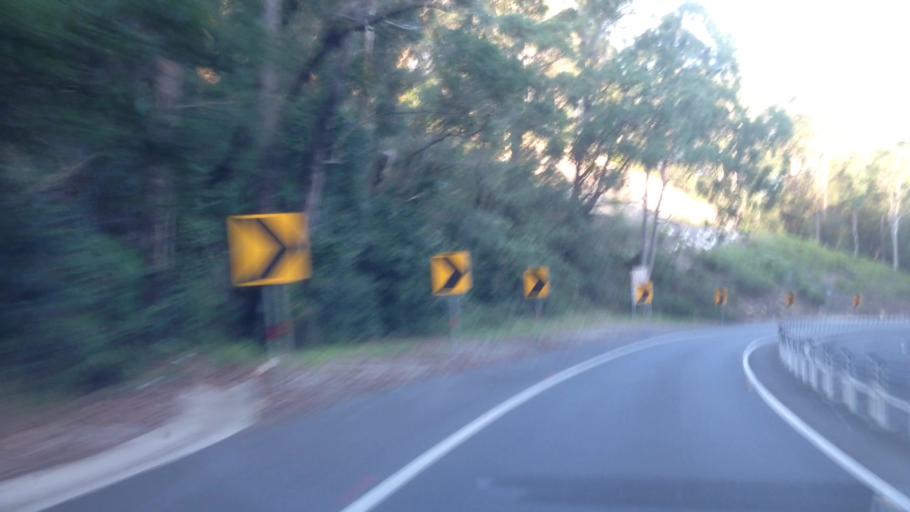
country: AU
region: New South Wales
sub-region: Lake Macquarie Shire
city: Cooranbong
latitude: -32.9699
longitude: 151.4819
